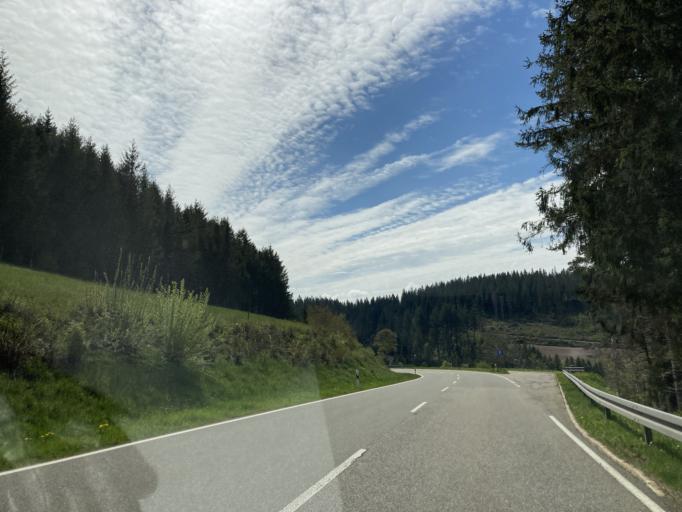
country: DE
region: Baden-Wuerttemberg
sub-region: Freiburg Region
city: Schonwald im Schwarzwald
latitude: 48.0824
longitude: 8.2055
